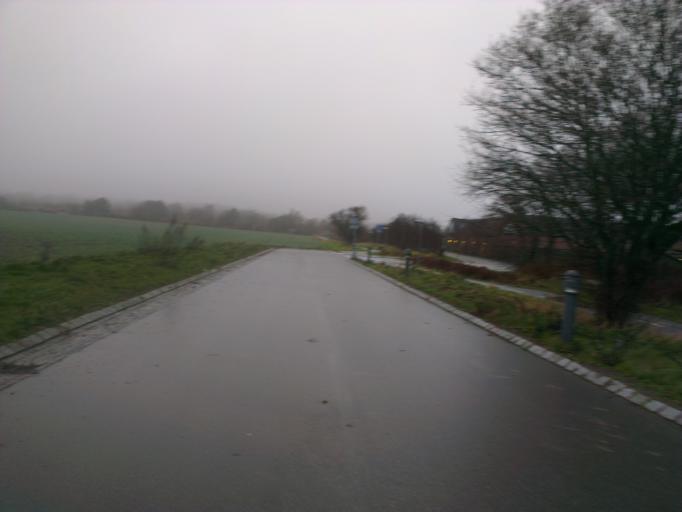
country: DK
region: Capital Region
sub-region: Frederikssund Kommune
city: Jaegerspris
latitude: 55.8493
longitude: 11.9842
